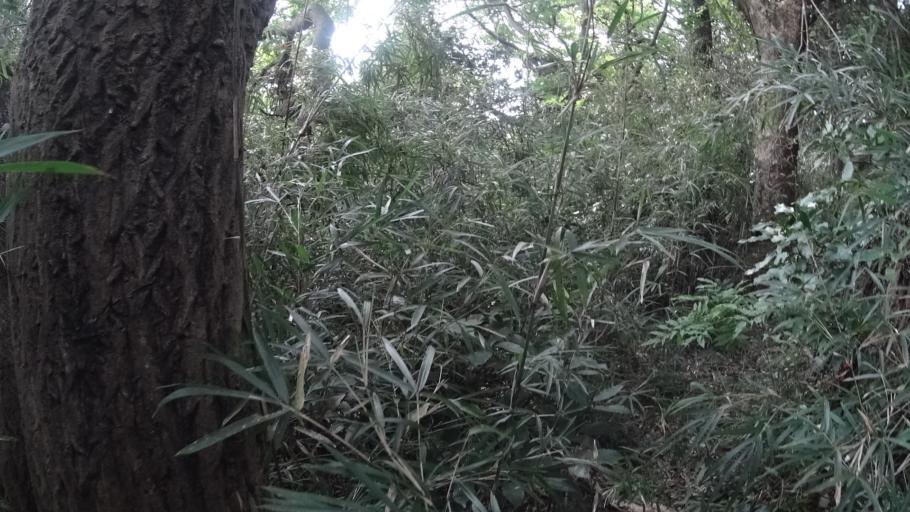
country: JP
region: Kanagawa
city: Zushi
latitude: 35.3558
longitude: 139.5972
